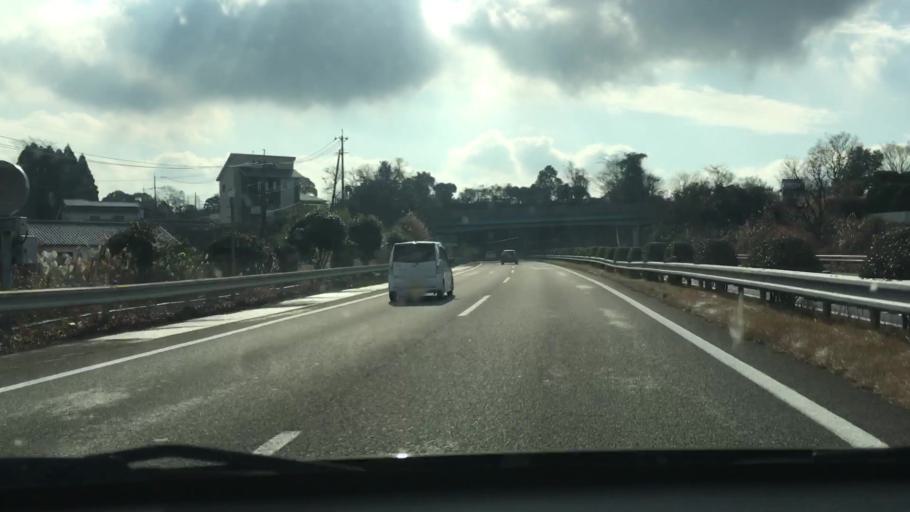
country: JP
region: Kumamoto
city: Uto
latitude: 32.6919
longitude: 130.7391
